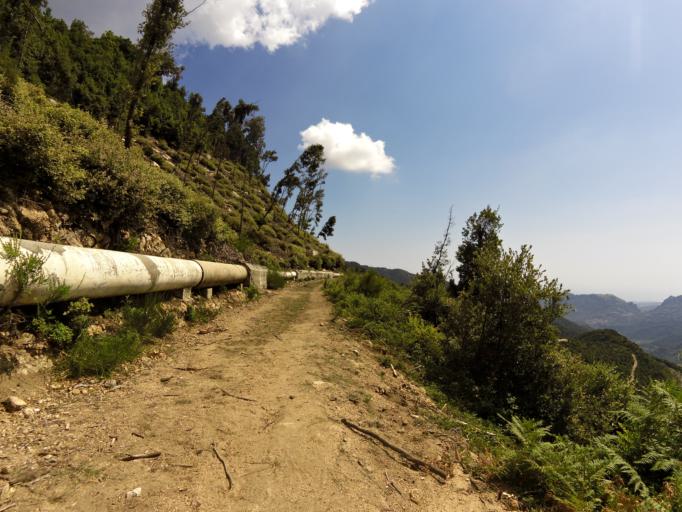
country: IT
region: Calabria
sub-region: Provincia di Vibo-Valentia
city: Nardodipace
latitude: 38.5077
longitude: 16.3921
